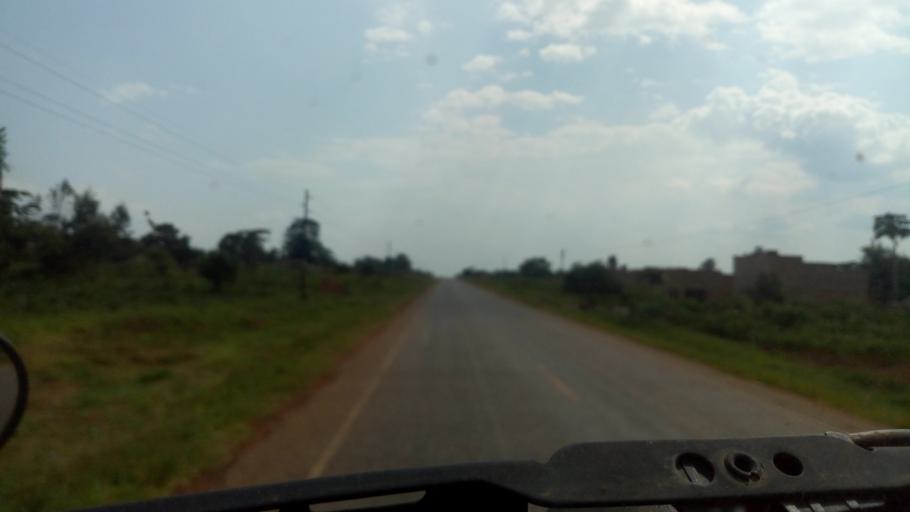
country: UG
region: Northern Region
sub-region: Oyam District
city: Oyam
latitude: 2.2173
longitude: 32.3931
